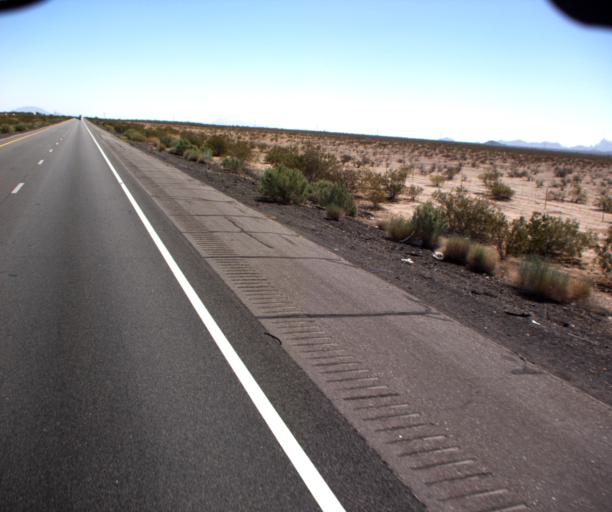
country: US
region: Arizona
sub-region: La Paz County
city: Salome
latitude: 33.5826
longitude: -113.4448
